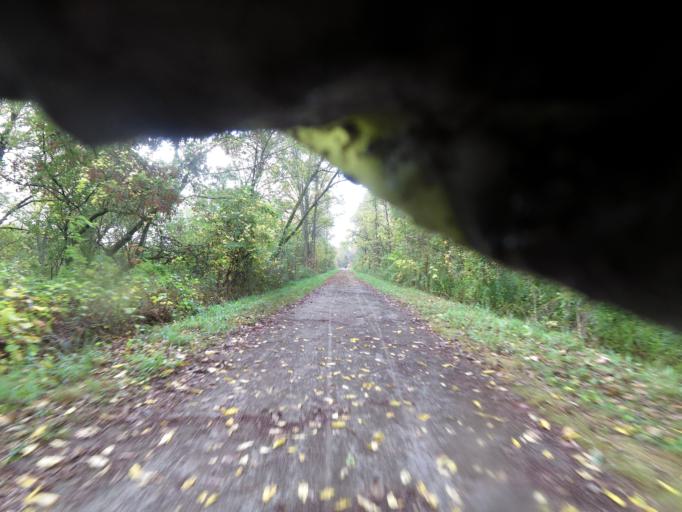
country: CA
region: Ontario
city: Brantford
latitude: 43.1412
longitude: -80.2178
